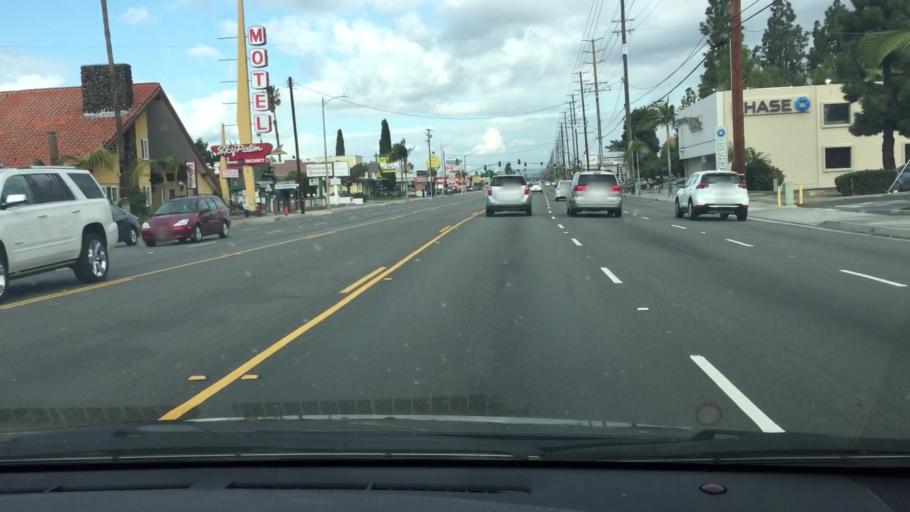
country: US
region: California
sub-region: Orange County
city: Orange
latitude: 33.7893
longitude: -117.8357
